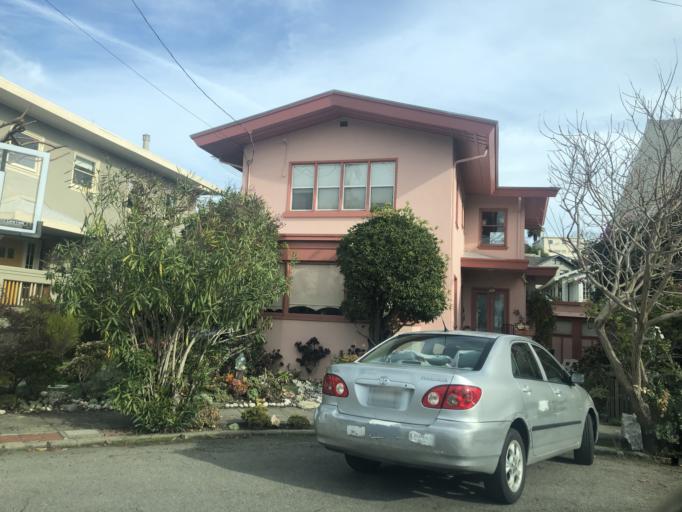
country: US
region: California
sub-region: Alameda County
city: Berkeley
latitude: 37.8520
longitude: -122.2496
